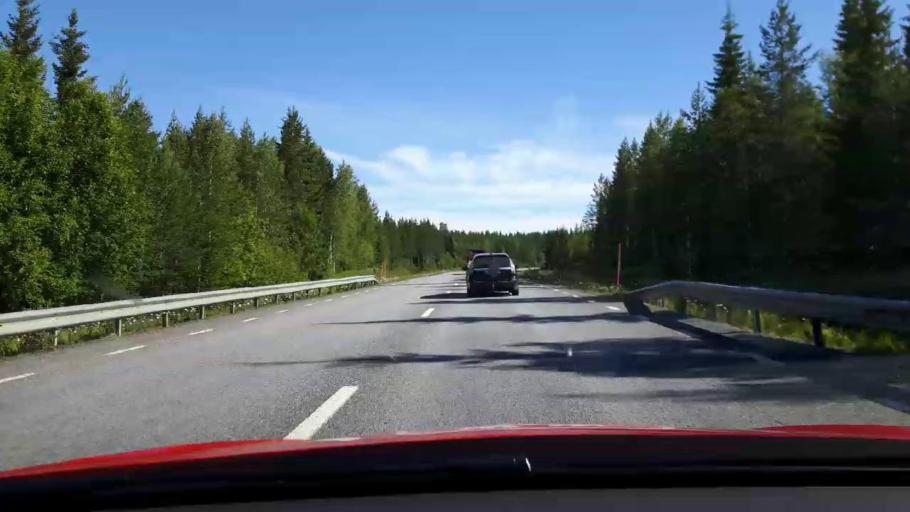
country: SE
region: Jaemtland
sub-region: OEstersunds Kommun
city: Lit
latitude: 63.3834
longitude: 14.8916
